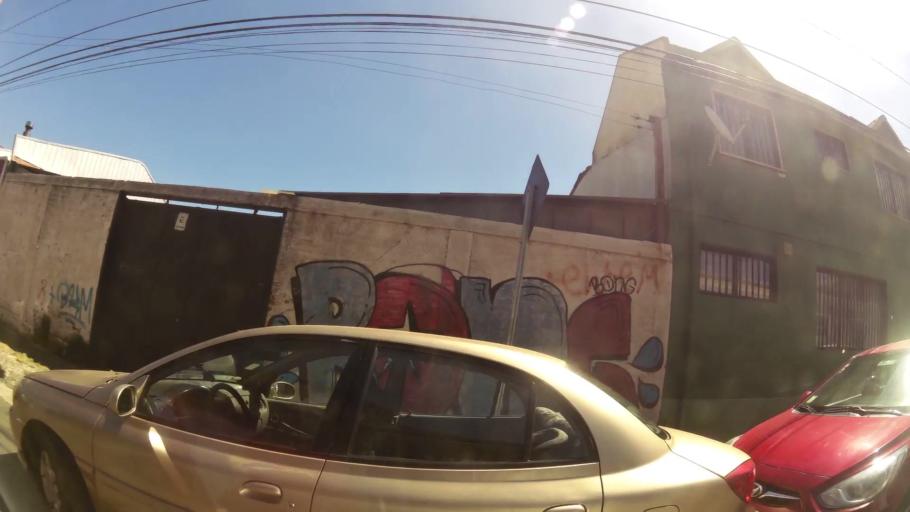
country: CL
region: Valparaiso
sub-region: Provincia de Valparaiso
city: Valparaiso
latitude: -33.0323
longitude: -71.6387
